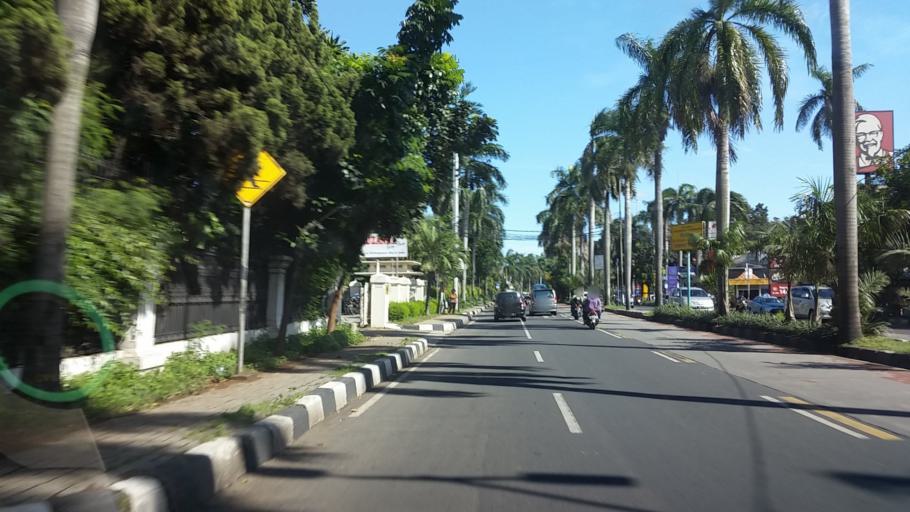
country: ID
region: Banten
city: South Tangerang
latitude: -6.2846
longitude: 106.7802
